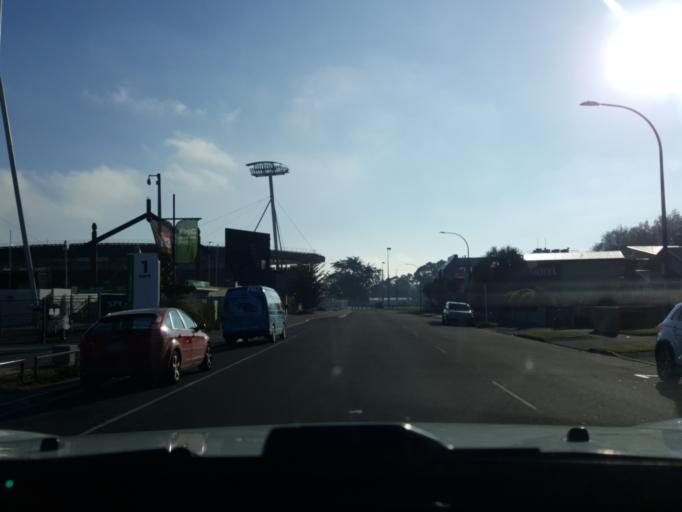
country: NZ
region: Waikato
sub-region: Hamilton City
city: Hamilton
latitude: -37.7810
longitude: 175.2703
